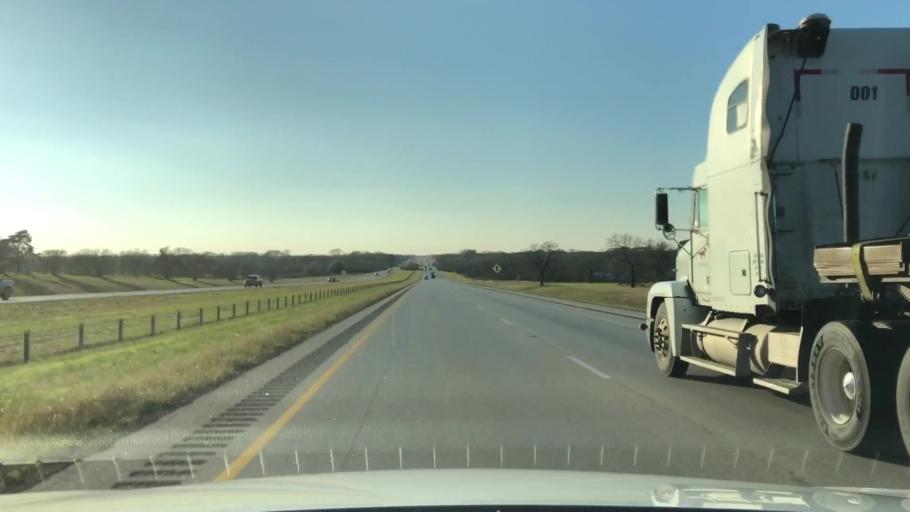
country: US
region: Texas
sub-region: Fayette County
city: Flatonia
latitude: 29.6921
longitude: -97.1770
